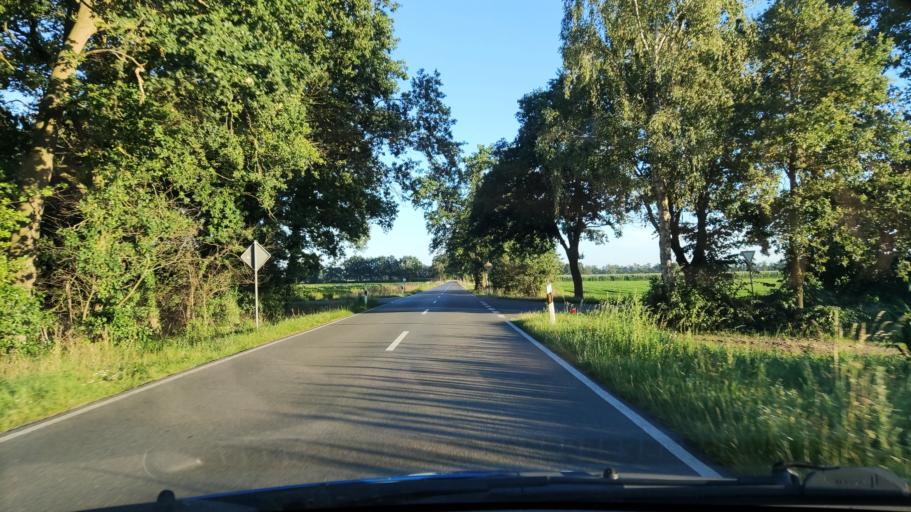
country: DE
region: Lower Saxony
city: Jameln
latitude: 53.0405
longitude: 11.1273
